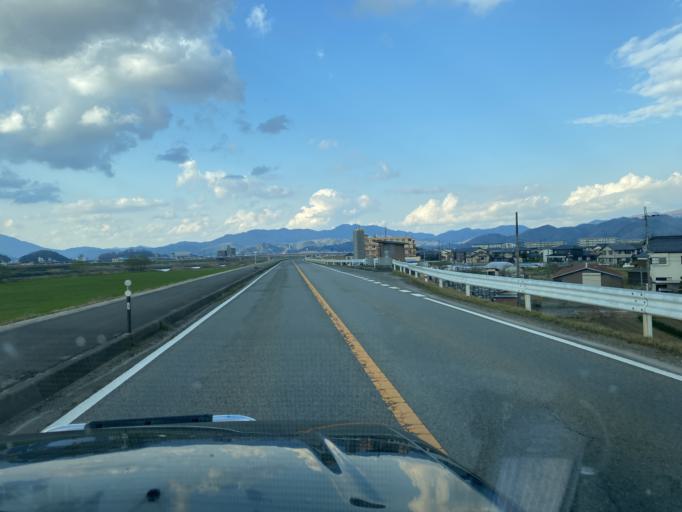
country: JP
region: Hyogo
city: Toyooka
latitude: 35.5181
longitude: 134.8243
